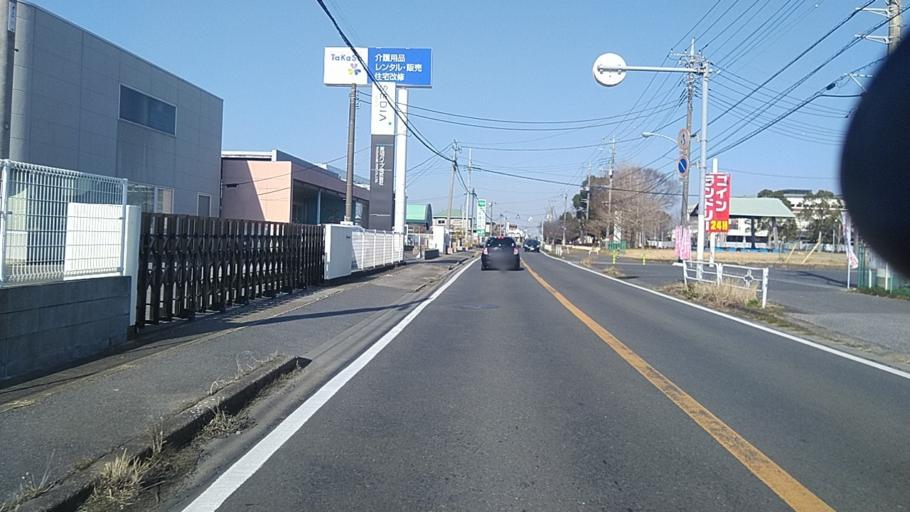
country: JP
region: Chiba
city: Mobara
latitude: 35.4368
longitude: 140.2937
